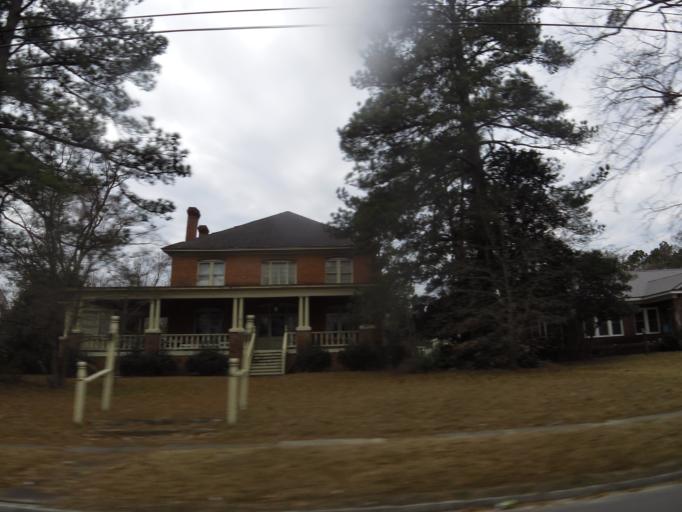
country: US
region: North Carolina
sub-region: Halifax County
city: Scotland Neck
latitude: 36.1367
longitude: -77.4217
